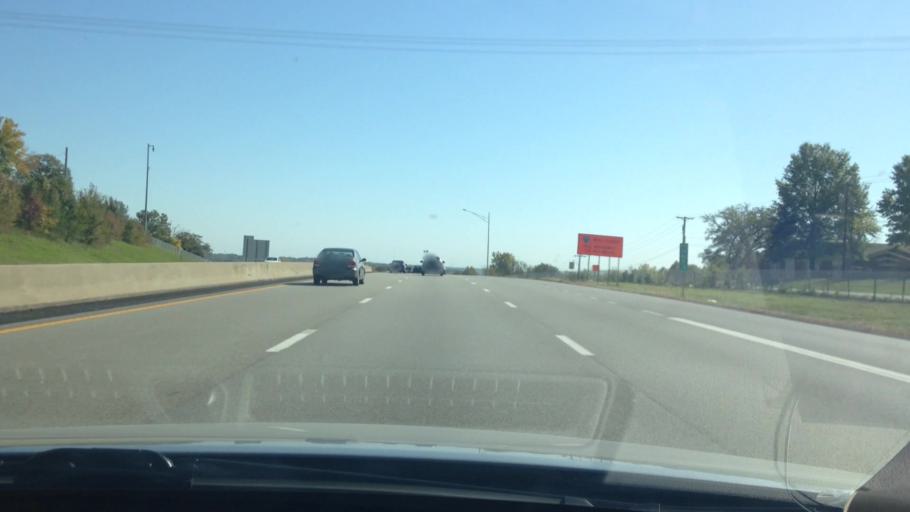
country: US
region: Missouri
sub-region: Platte County
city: Riverside
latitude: 39.2074
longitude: -94.6361
